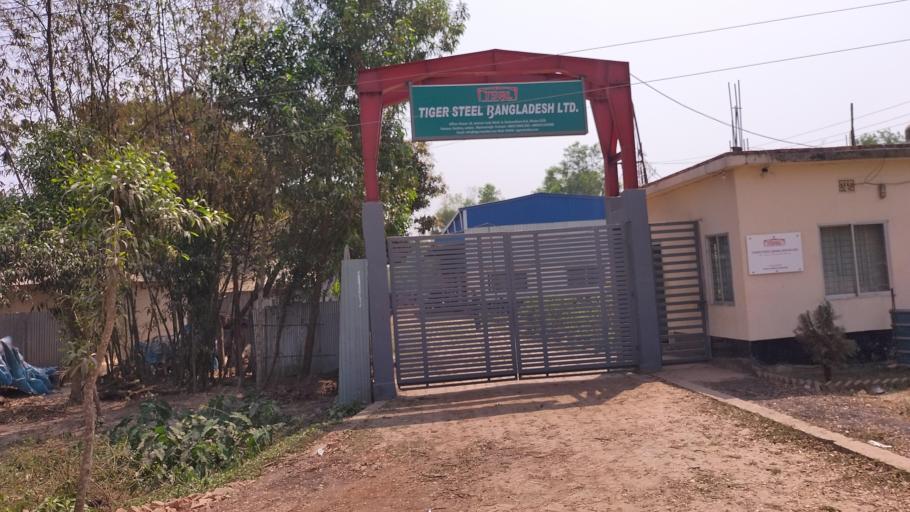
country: BD
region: Dhaka
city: Sakhipur
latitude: 24.3077
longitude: 90.3155
